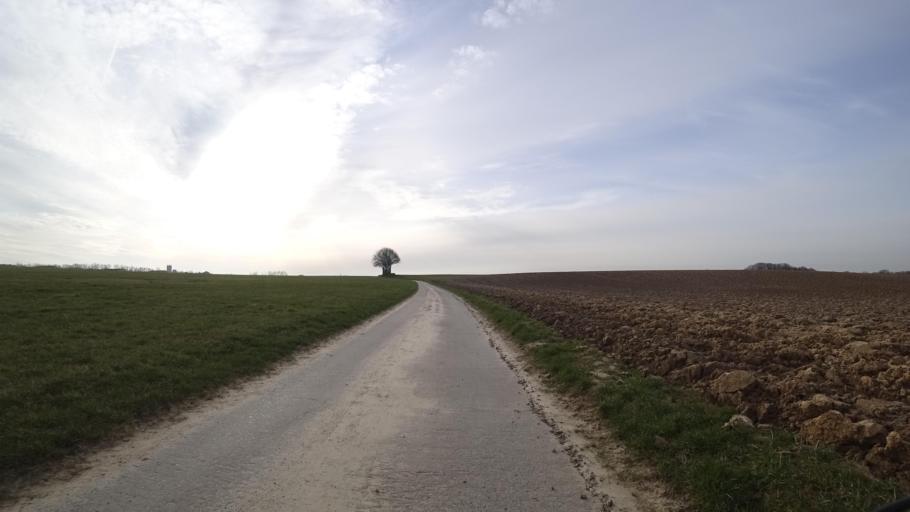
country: BE
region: Wallonia
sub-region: Province du Brabant Wallon
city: Chaumont-Gistoux
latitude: 50.6732
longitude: 4.7060
